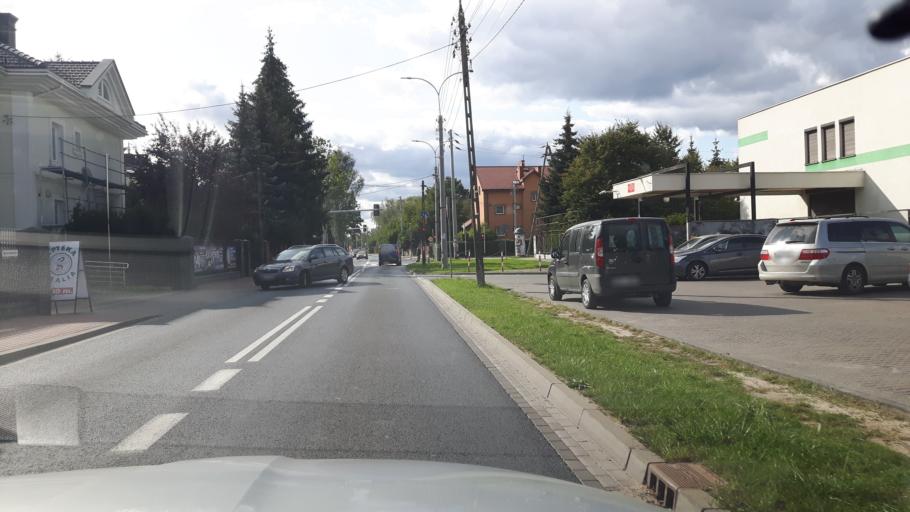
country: PL
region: Masovian Voivodeship
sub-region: Powiat wolominski
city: Kobylka
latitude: 52.3418
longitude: 21.2137
